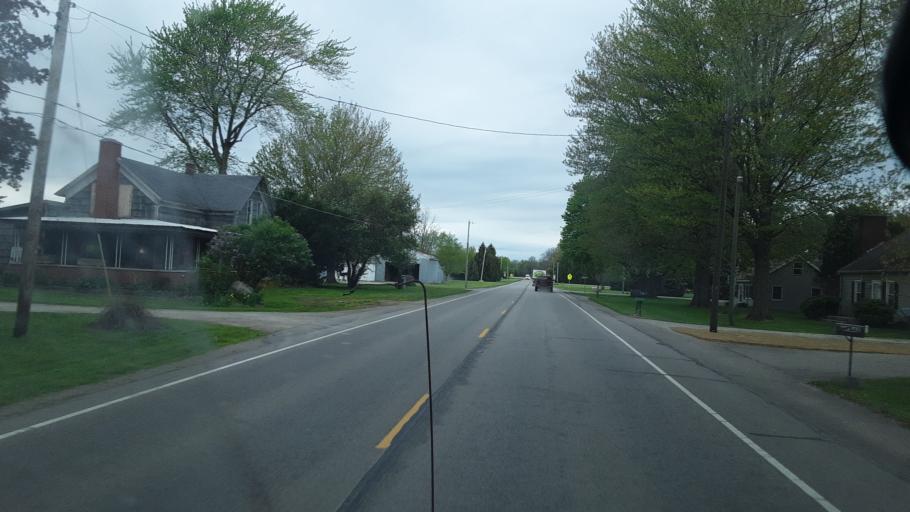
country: US
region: Indiana
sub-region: Elkhart County
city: New Paris
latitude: 41.5121
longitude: -85.7639
